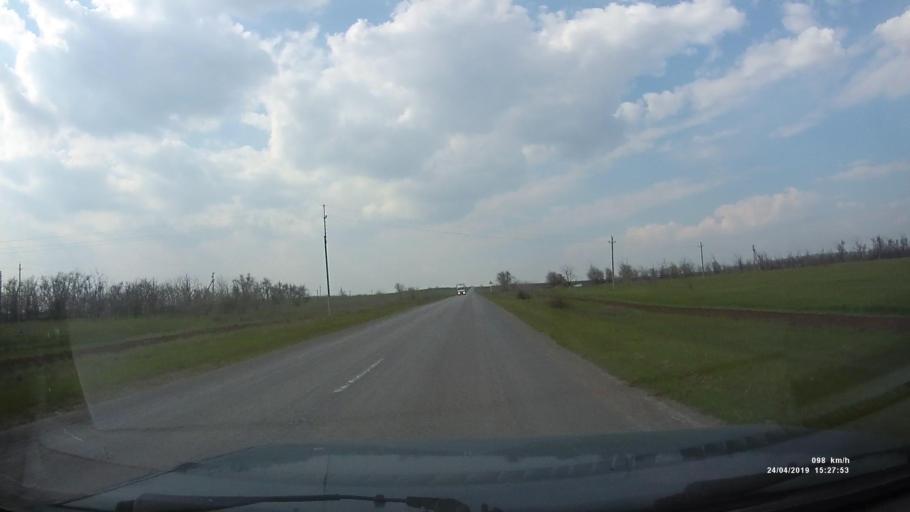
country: RU
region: Rostov
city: Remontnoye
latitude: 46.5710
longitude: 43.0226
